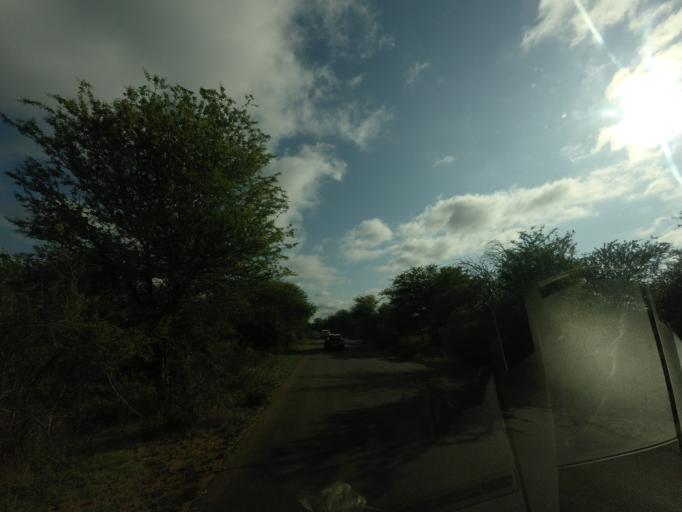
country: ZA
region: Mpumalanga
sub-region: Ehlanzeni District
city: Komatipoort
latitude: -25.2227
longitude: 31.8616
